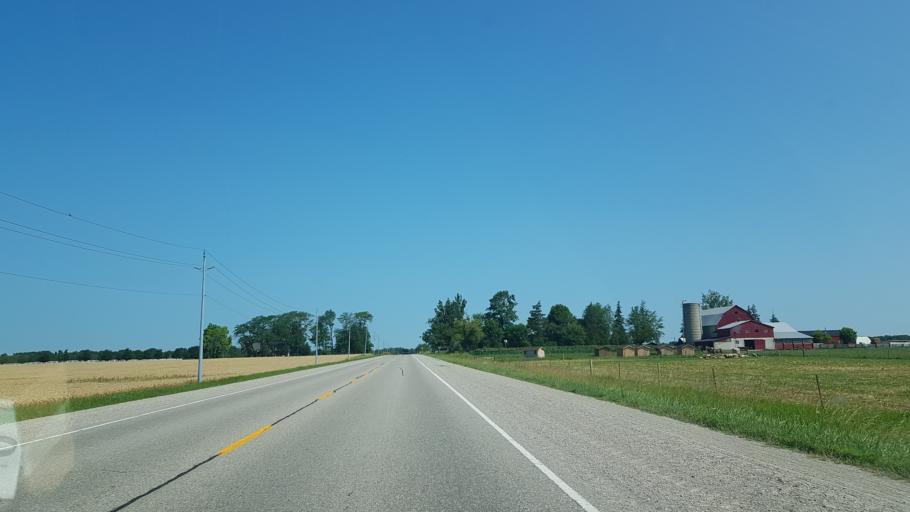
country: CA
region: Ontario
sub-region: Oxford County
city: Woodstock
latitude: 42.9386
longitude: -80.6775
